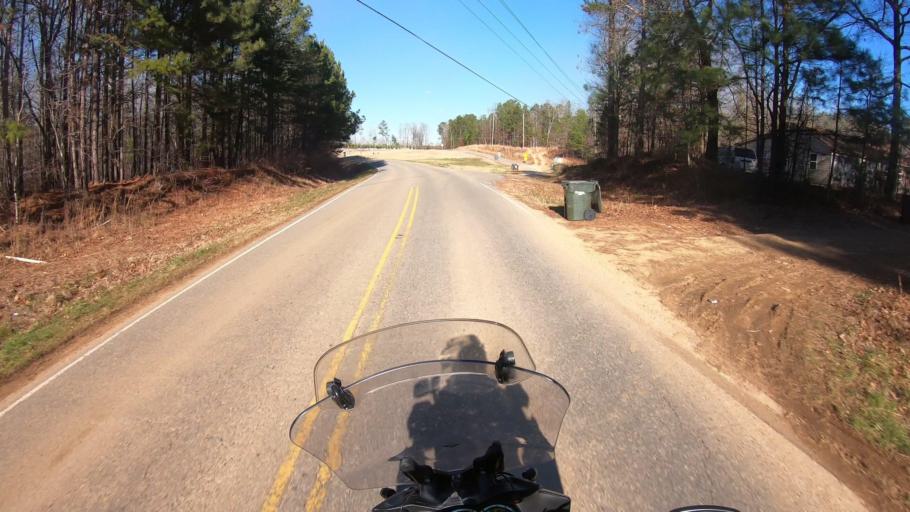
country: US
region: Alabama
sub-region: Cleburne County
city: Heflin
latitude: 33.7326
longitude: -85.4777
